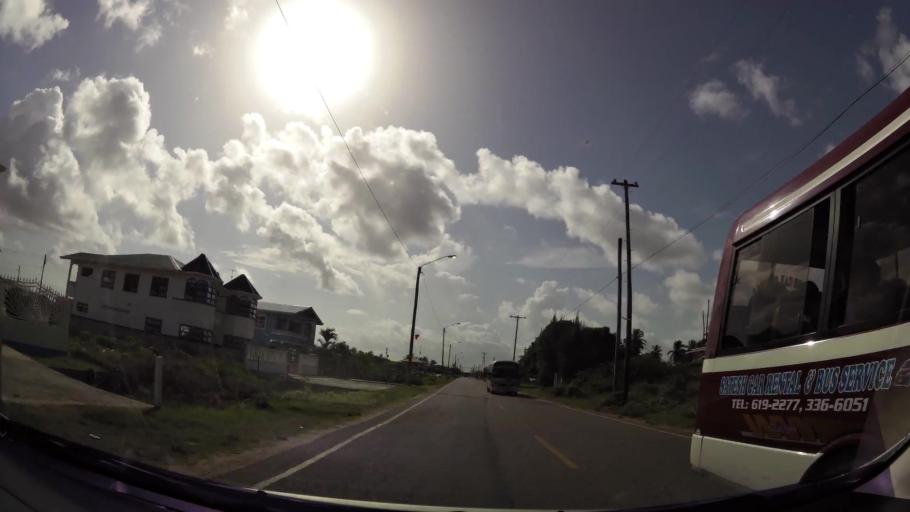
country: GY
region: Demerara-Mahaica
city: Mahaica Village
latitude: 6.7478
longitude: -57.9644
